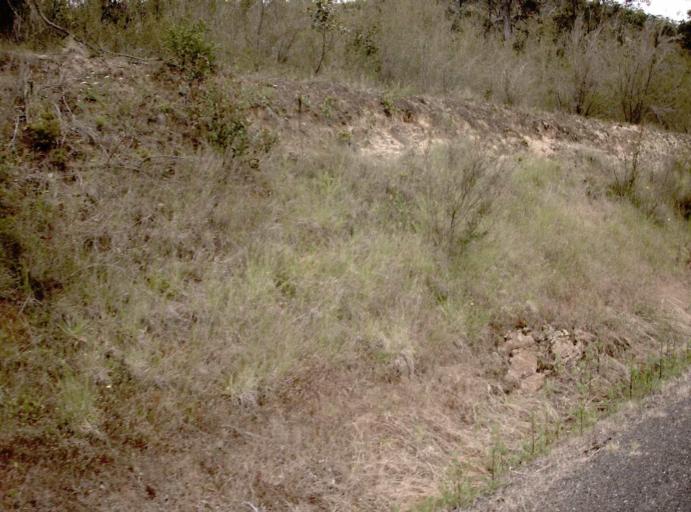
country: AU
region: New South Wales
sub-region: Bombala
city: Bombala
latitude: -37.2404
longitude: 149.2609
